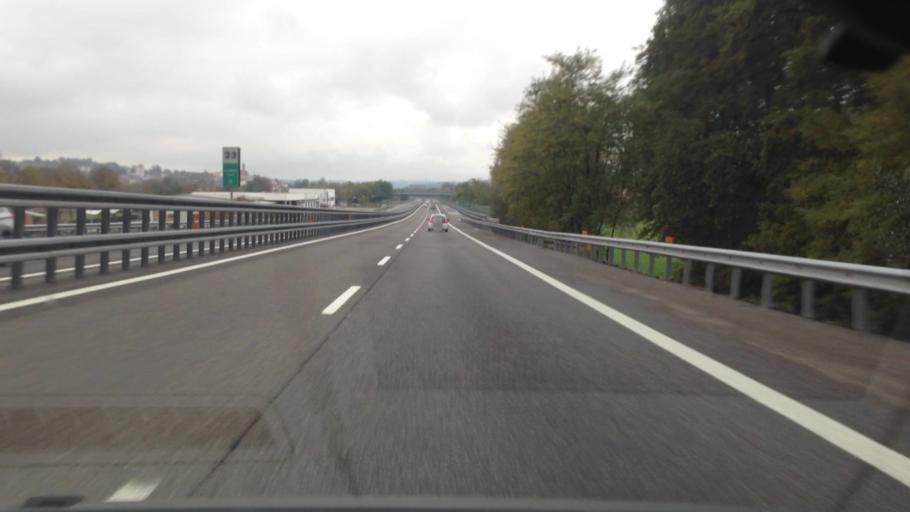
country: IT
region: Piedmont
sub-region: Provincia di Asti
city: Castellero
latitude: 44.9046
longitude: 8.0571
